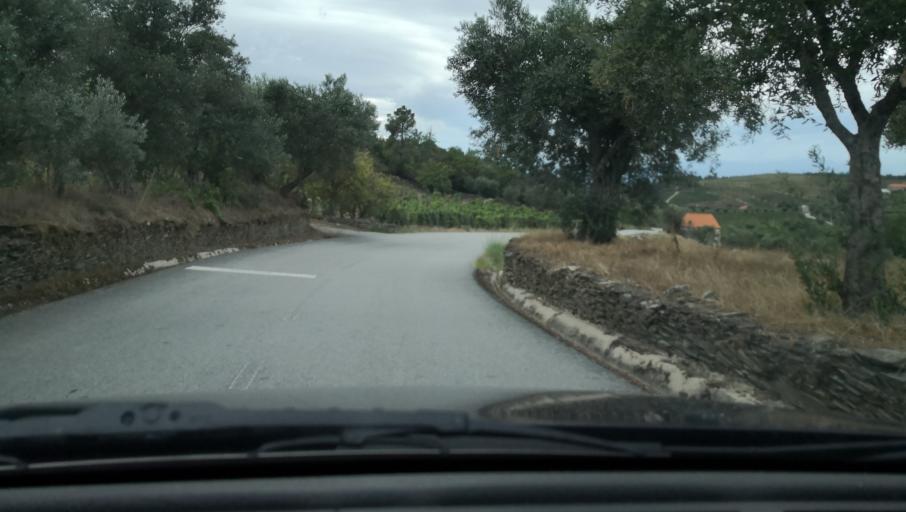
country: PT
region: Viseu
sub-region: Tabuaco
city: Tabuaco
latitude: 41.1255
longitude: -7.5909
